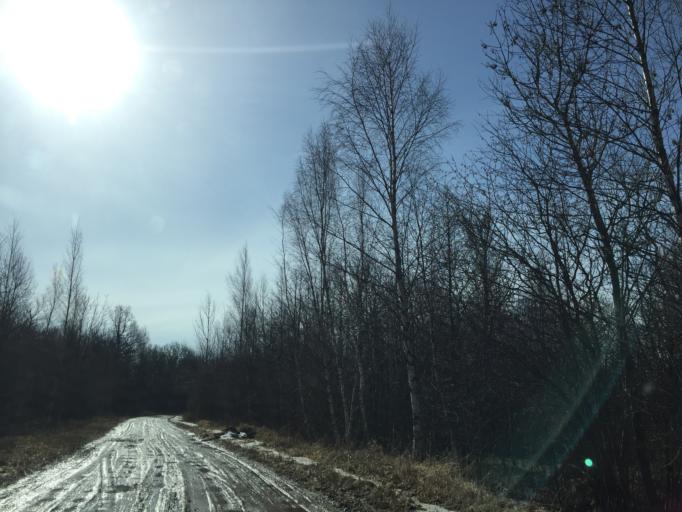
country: EE
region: Laeaene
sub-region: Haapsalu linn
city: Haapsalu
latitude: 58.6571
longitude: 23.5138
